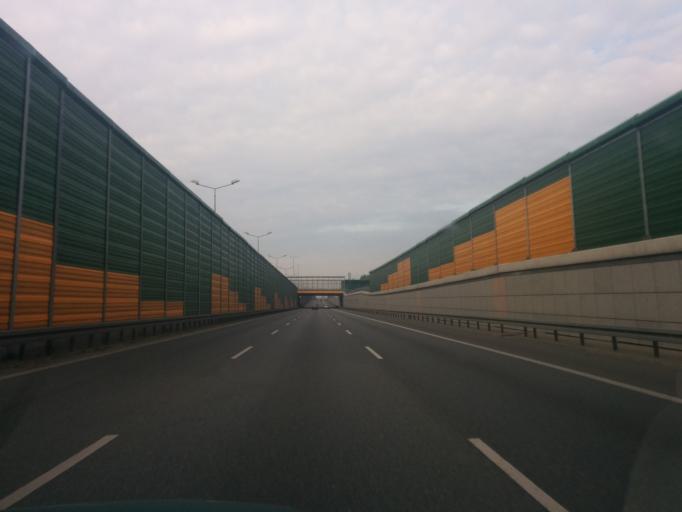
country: PL
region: Masovian Voivodeship
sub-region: Warszawa
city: Bemowo
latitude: 52.2470
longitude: 20.9182
